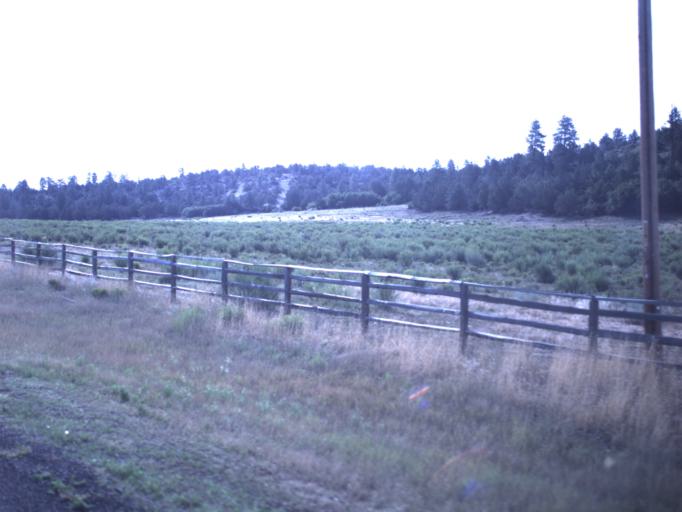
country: US
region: Utah
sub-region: Washington County
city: Hildale
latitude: 37.2403
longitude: -112.8254
